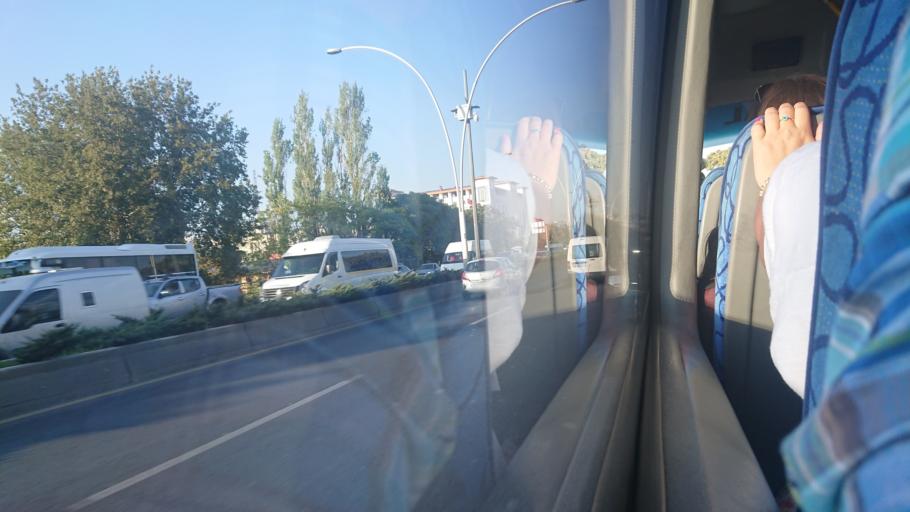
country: TR
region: Ankara
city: Ankara
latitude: 39.9457
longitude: 32.8310
